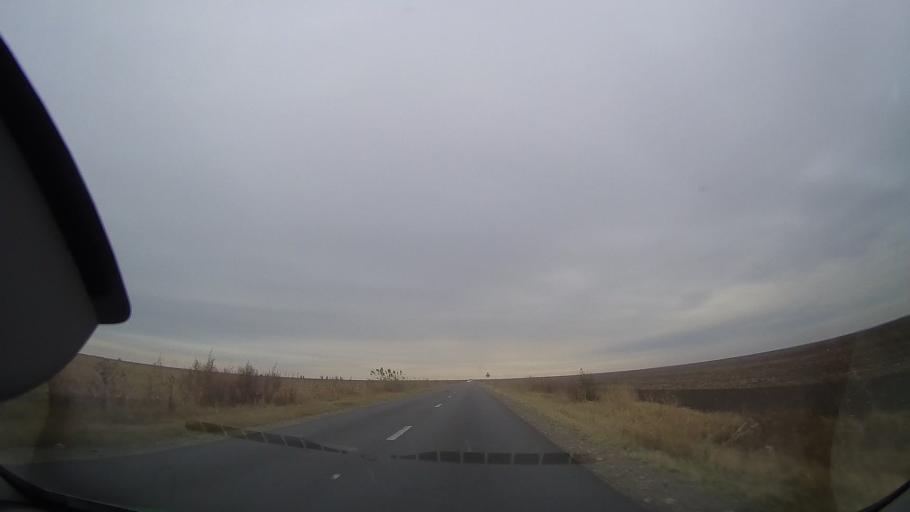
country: RO
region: Ialomita
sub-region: Oras Amara
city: Amara
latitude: 44.6459
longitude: 27.3005
